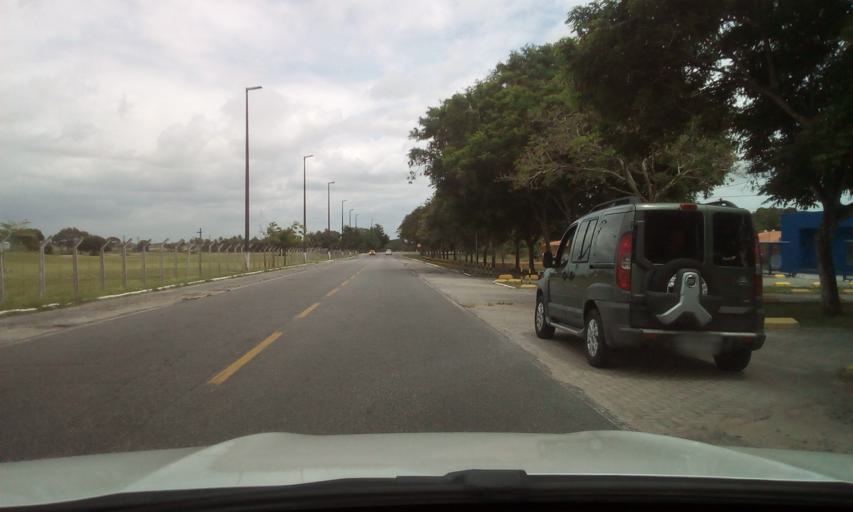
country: BR
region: Paraiba
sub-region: Bayeux
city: Bayeux
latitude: -7.1439
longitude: -34.9477
